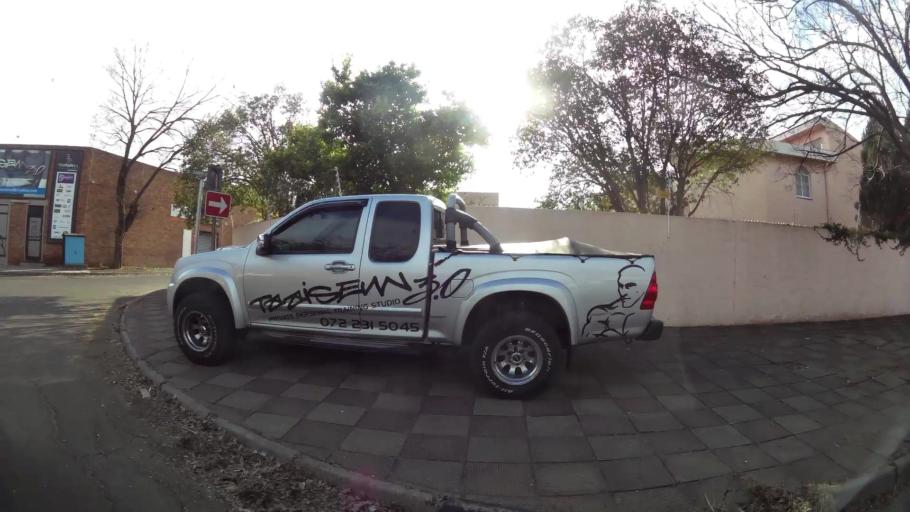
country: ZA
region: Orange Free State
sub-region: Mangaung Metropolitan Municipality
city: Bloemfontein
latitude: -29.1212
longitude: 26.1748
